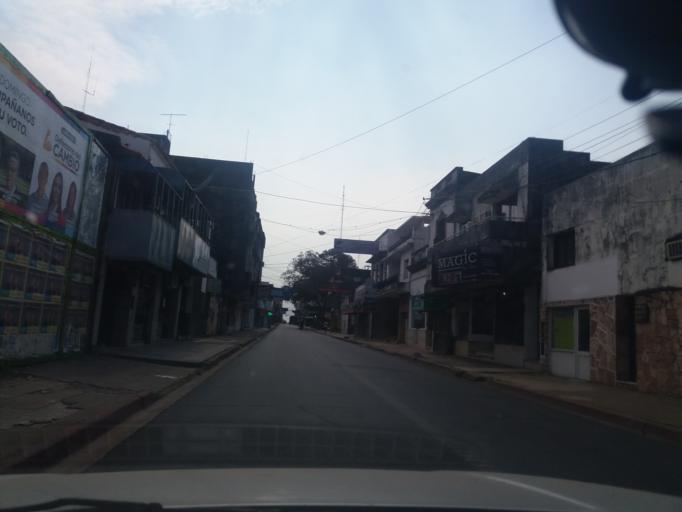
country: AR
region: Corrientes
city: Corrientes
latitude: -27.4684
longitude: -58.8382
